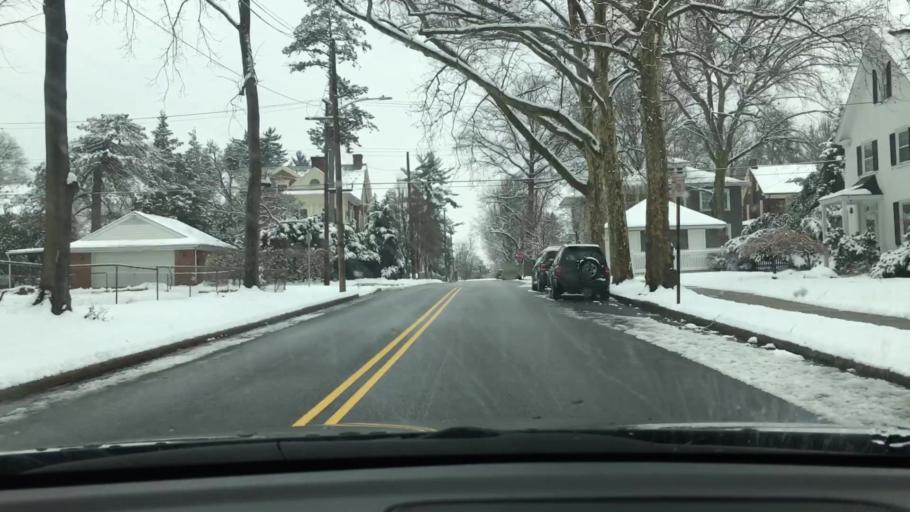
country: US
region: Pennsylvania
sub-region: York County
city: Grantley
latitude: 39.9499
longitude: -76.7200
